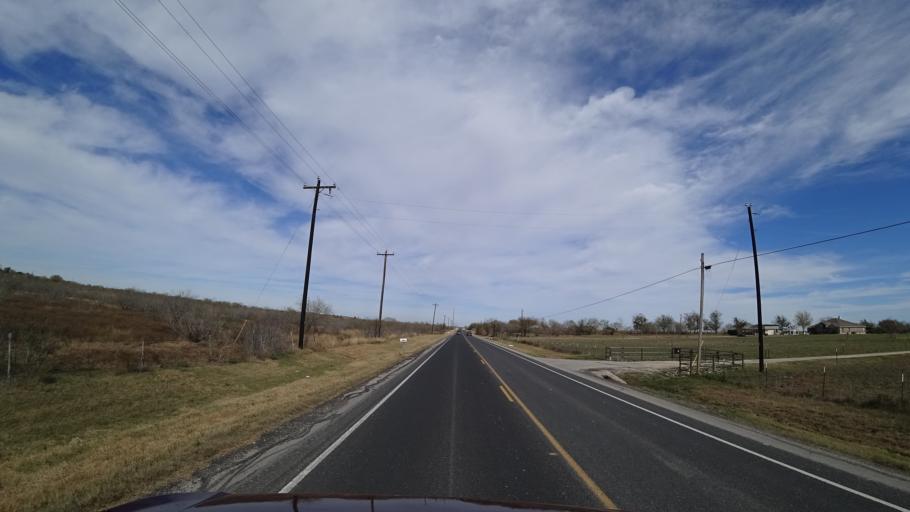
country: US
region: Texas
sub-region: Travis County
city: Onion Creek
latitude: 30.1258
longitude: -97.7122
